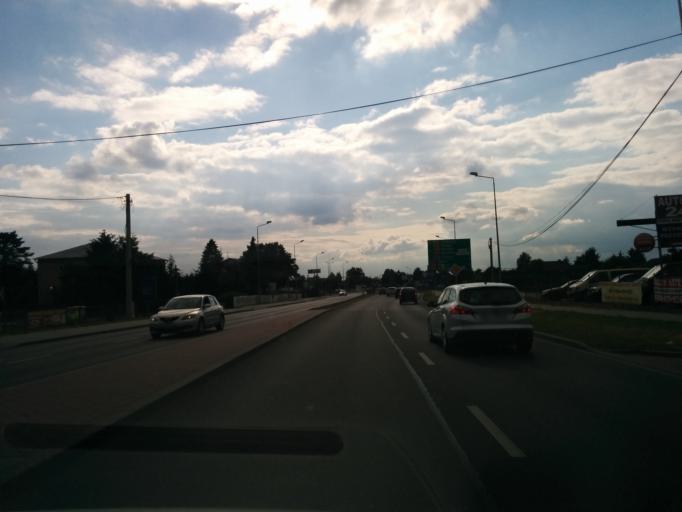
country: PL
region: Masovian Voivodeship
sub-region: Warszawa
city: Bemowo
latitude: 52.2400
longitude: 20.8923
